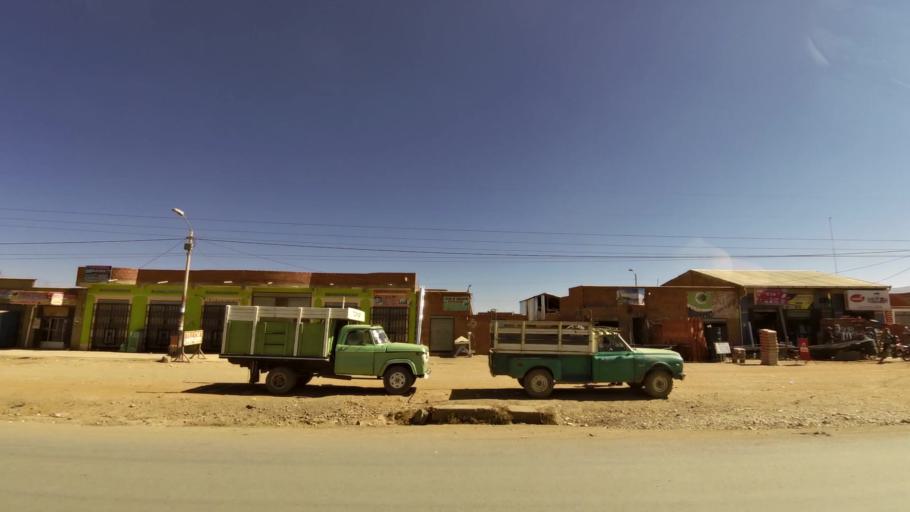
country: BO
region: La Paz
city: La Paz
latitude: -16.5764
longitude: -68.2294
